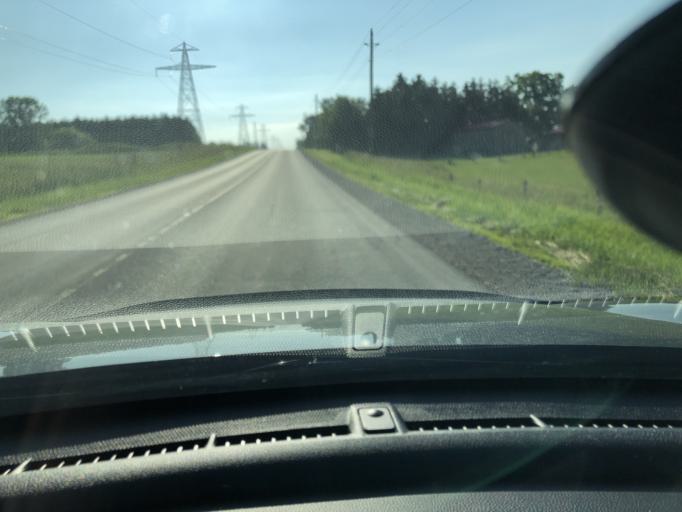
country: CA
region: Ontario
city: Stratford
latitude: 43.3885
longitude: -80.8951
